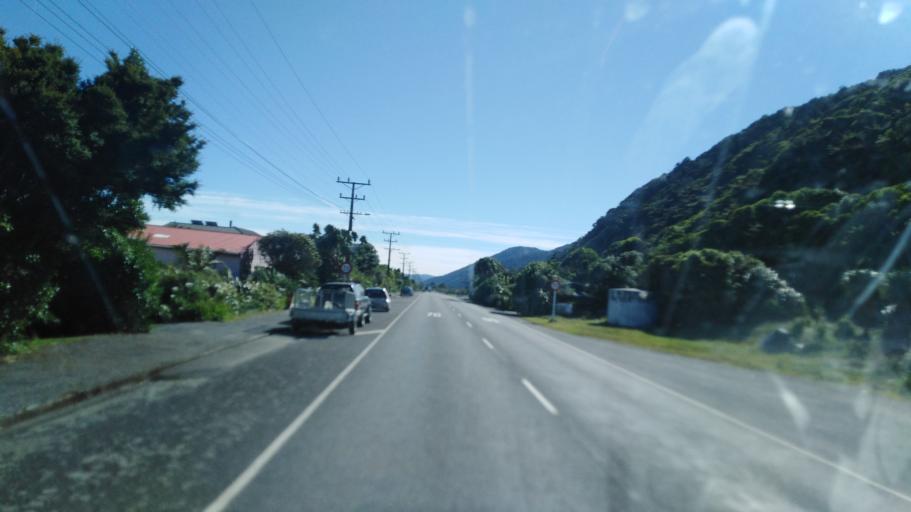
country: NZ
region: West Coast
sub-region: Buller District
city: Westport
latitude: -41.6253
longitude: 171.8579
